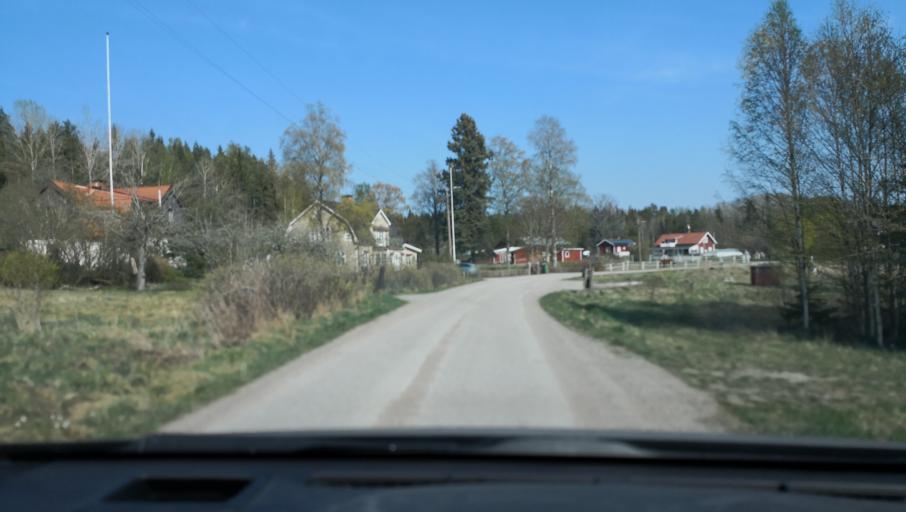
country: SE
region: Vaestmanland
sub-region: Sala Kommun
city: Sala
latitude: 60.0073
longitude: 16.7036
